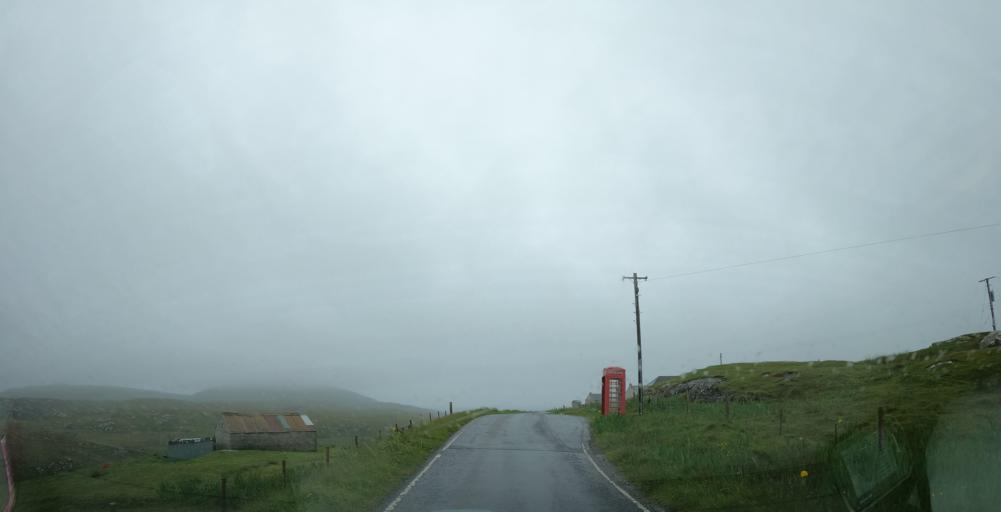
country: GB
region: Scotland
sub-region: Eilean Siar
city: Barra
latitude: 56.9869
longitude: -7.4118
